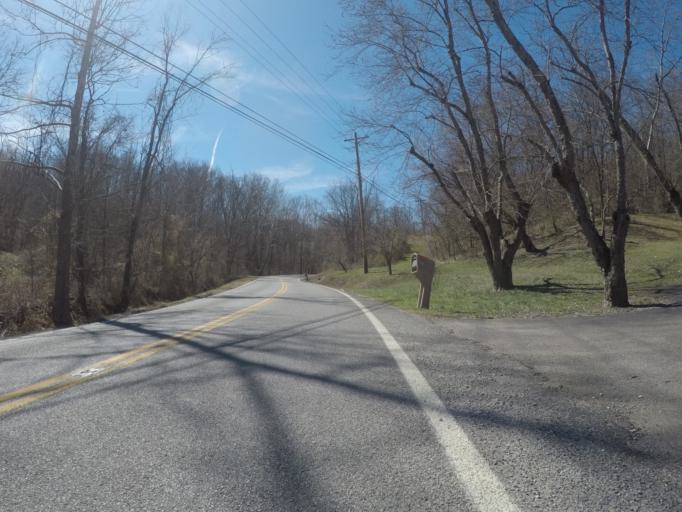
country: US
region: Ohio
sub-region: Lawrence County
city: Burlington
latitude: 38.4914
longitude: -82.5419
